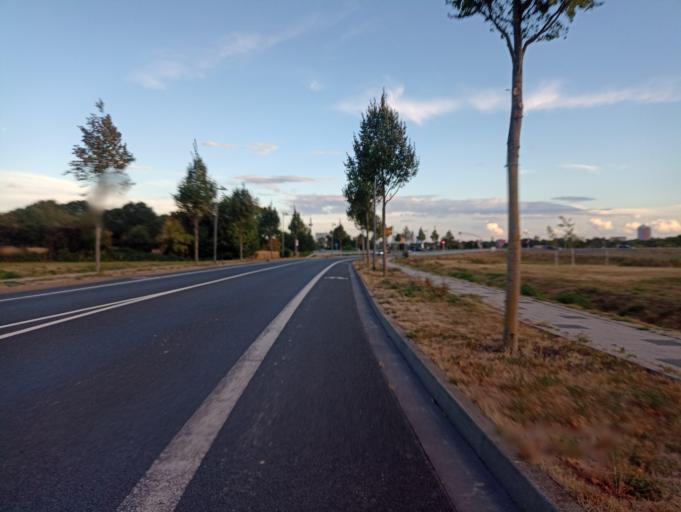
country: DE
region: Hesse
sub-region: Regierungsbezirk Darmstadt
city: Steinbach am Taunus
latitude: 50.1745
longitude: 8.6165
